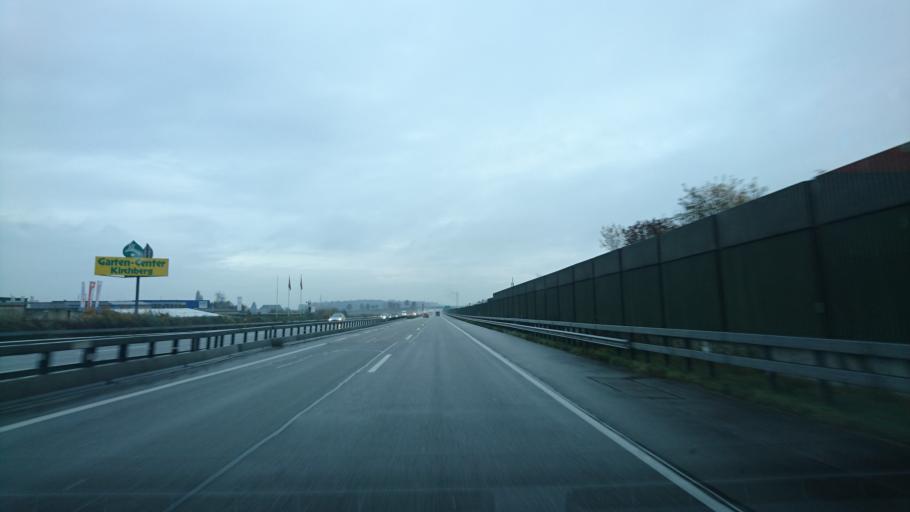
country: CH
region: Bern
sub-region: Emmental District
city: Kirchberg
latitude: 47.0935
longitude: 7.5733
